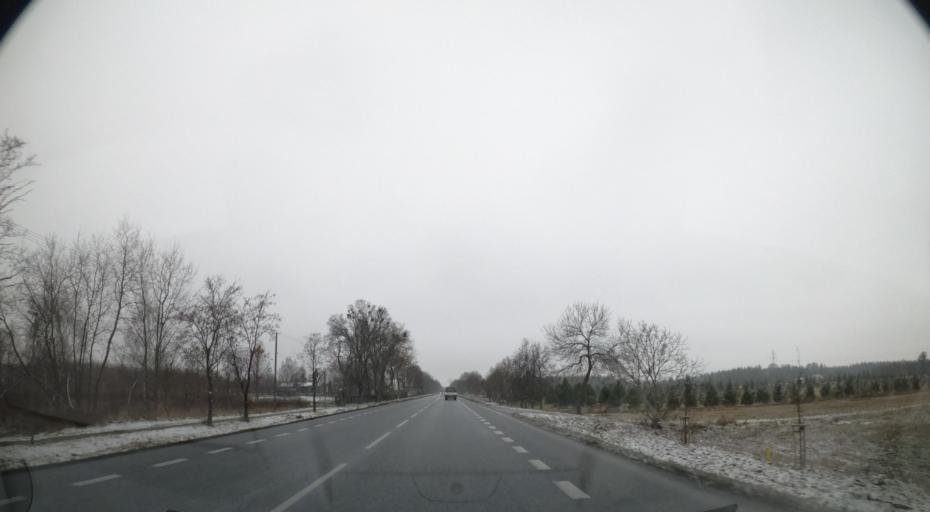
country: PL
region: Masovian Voivodeship
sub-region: Powiat warszawski zachodni
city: Bieniewice
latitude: 52.2012
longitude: 20.5546
